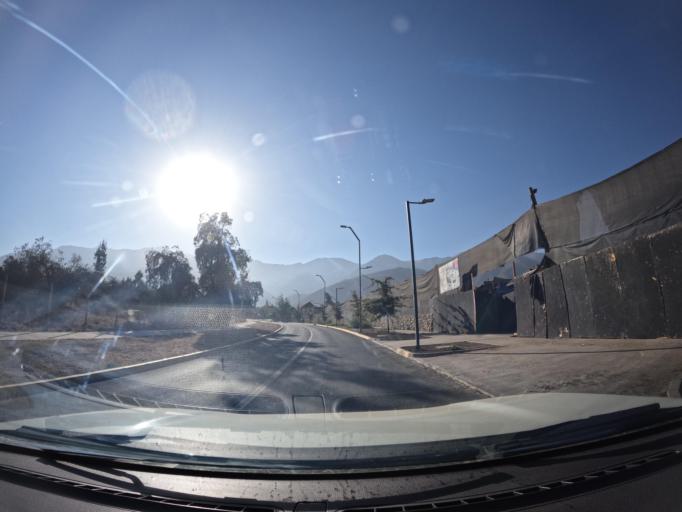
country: CL
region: Santiago Metropolitan
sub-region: Provincia de Santiago
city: Villa Presidente Frei, Nunoa, Santiago, Chile
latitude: -33.5034
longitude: -70.5313
